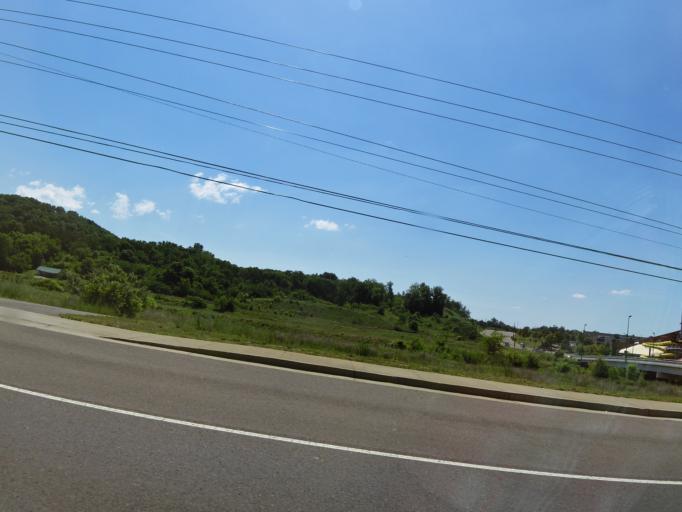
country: US
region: Tennessee
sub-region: Sevier County
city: Sevierville
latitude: 35.8918
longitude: -83.5809
